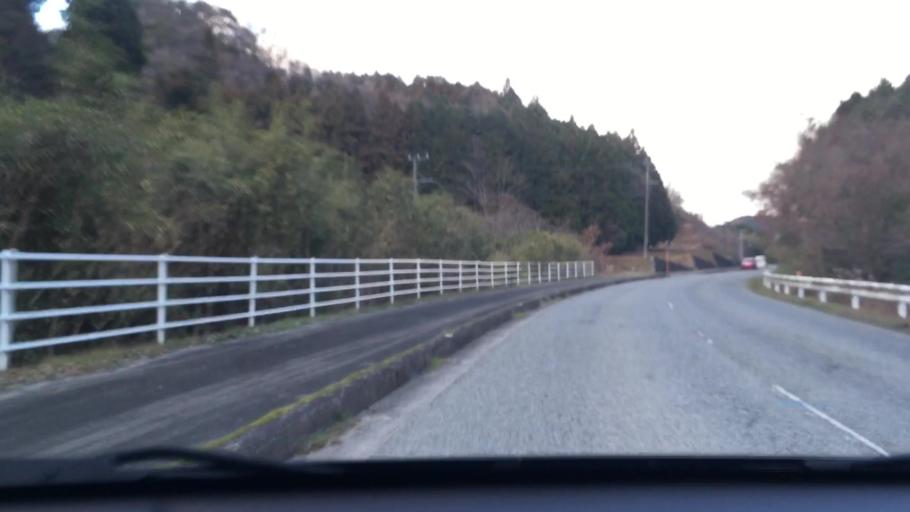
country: JP
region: Oita
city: Bungo-Takada-shi
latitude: 33.4734
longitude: 131.3842
